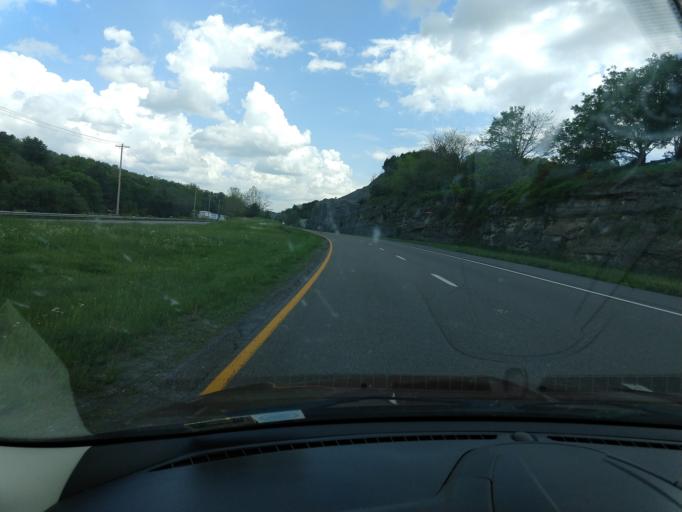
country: US
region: Virginia
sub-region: Tazewell County
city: Claypool Hill
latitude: 37.0423
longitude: -81.7893
